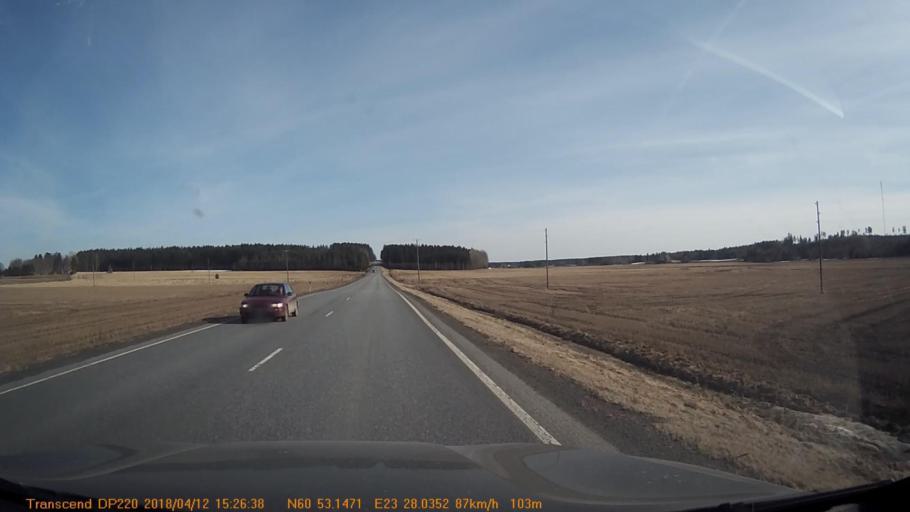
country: FI
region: Haeme
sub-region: Forssa
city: Jokioinen
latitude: 60.8851
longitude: 23.4687
